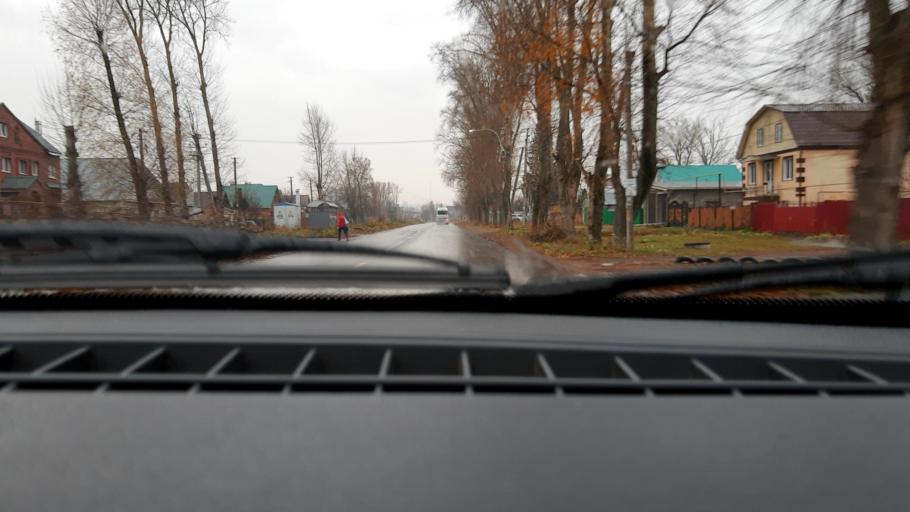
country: RU
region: Bashkortostan
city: Mikhaylovka
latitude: 54.7643
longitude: 55.8986
